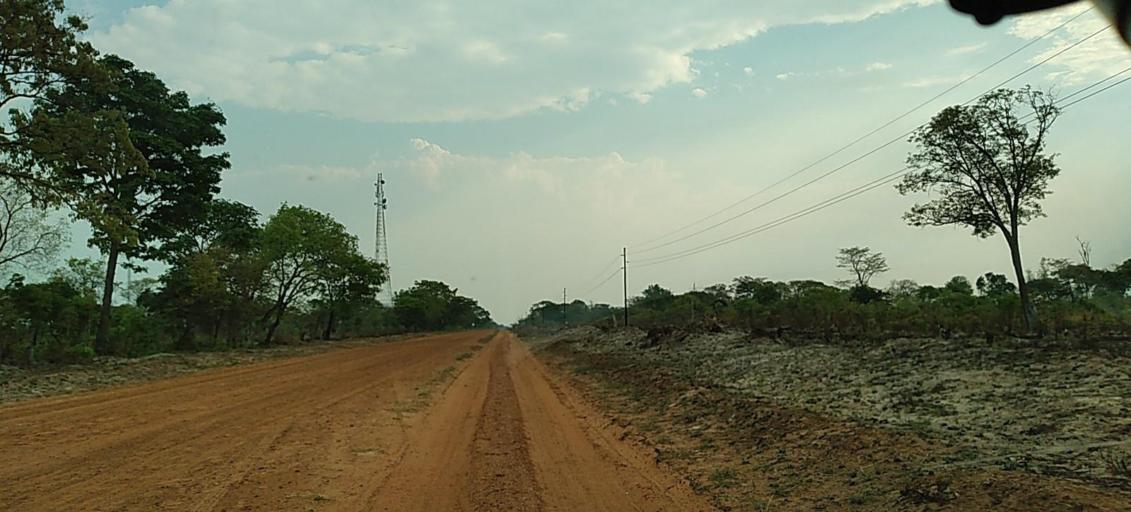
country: ZM
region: North-Western
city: Kabompo
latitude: -13.8828
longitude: 23.6630
